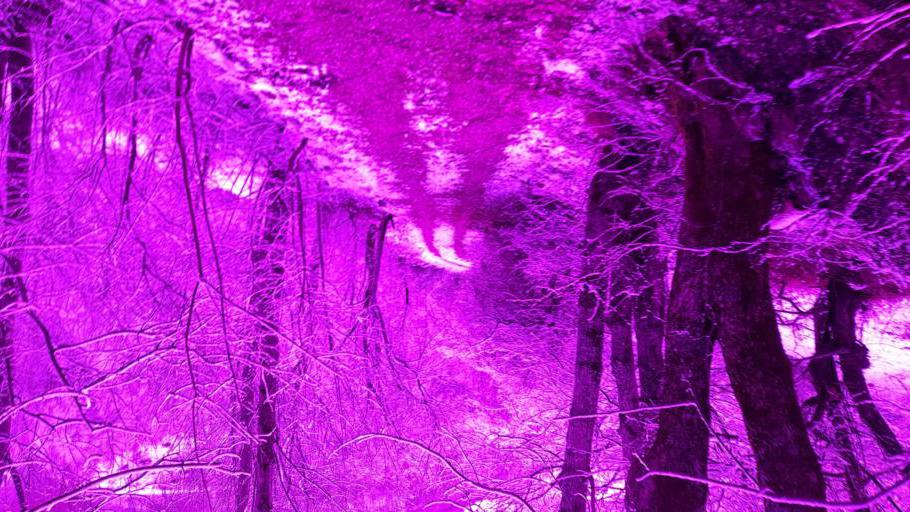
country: IT
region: The Marches
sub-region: Provincia di Macerata
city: Bolognola
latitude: 42.9874
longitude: 13.2308
